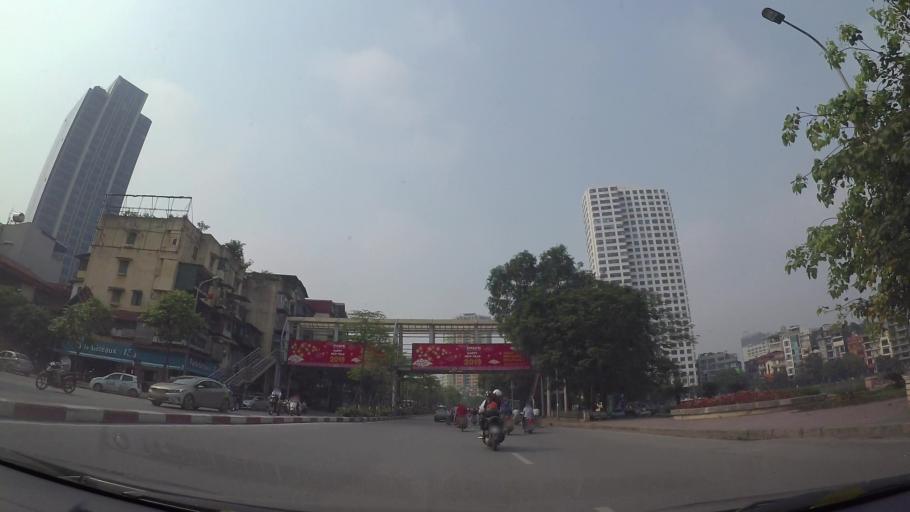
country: VN
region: Ha Noi
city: Cau Giay
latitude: 21.0277
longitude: 105.8122
